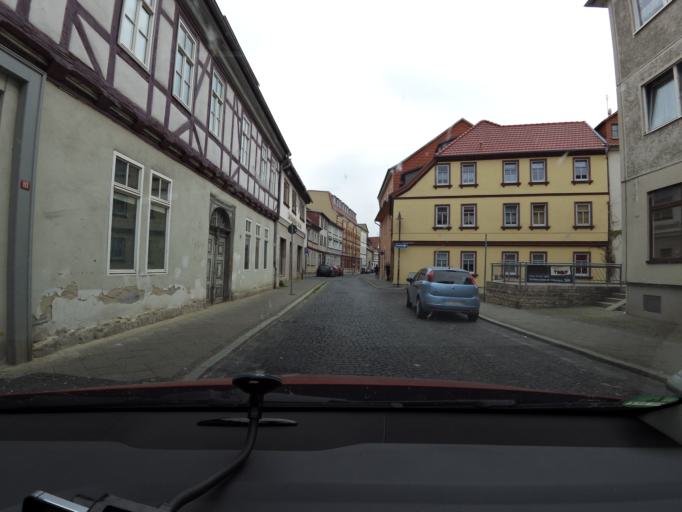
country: DE
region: Thuringia
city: Muehlhausen
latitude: 51.2090
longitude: 10.4542
